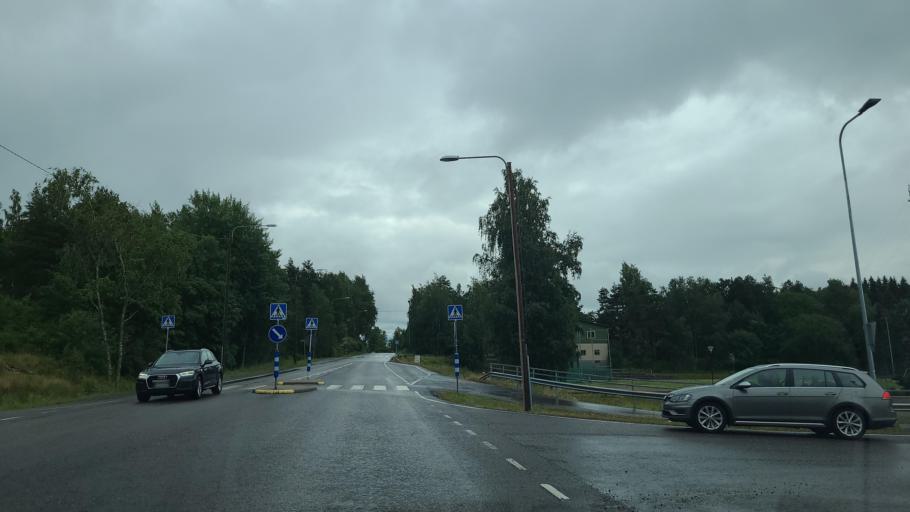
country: FI
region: Varsinais-Suomi
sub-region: Aboland-Turunmaa
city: Kimito
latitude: 60.1726
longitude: 22.7345
